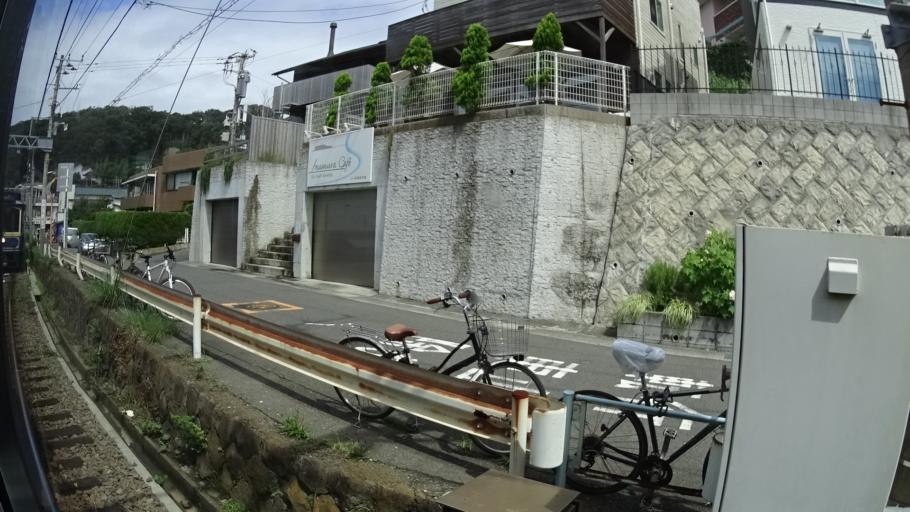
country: JP
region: Kanagawa
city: Kamakura
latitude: 35.3043
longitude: 139.5229
